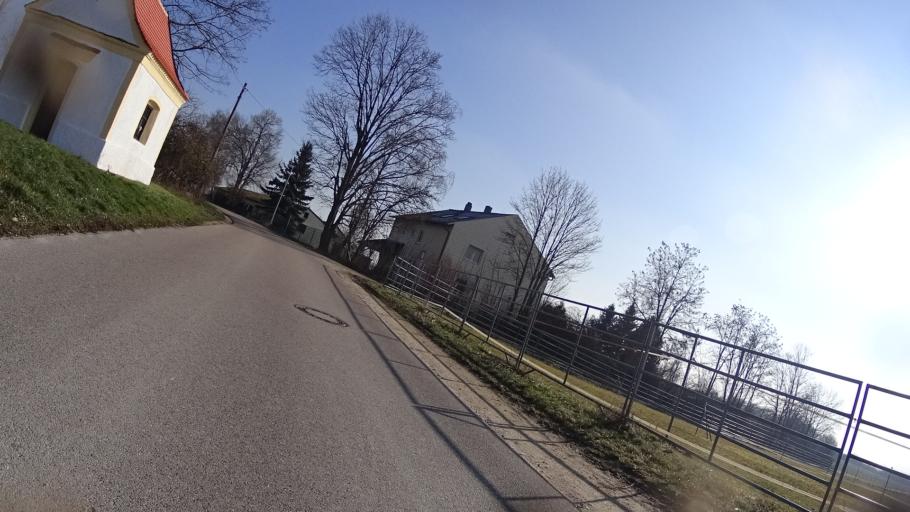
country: DE
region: Bavaria
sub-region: Upper Bavaria
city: Wettstetten
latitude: 48.8273
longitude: 11.3889
